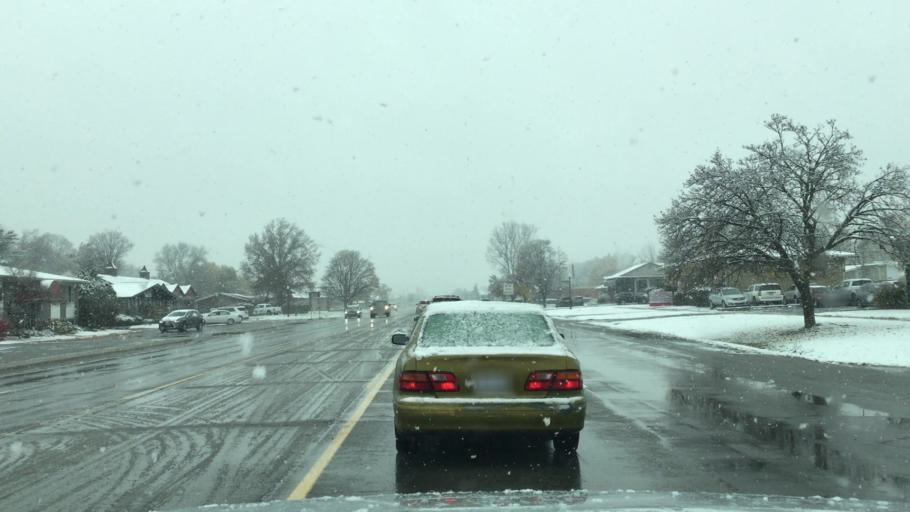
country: US
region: Michigan
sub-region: Oakland County
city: Lathrup Village
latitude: 42.4962
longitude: -83.2222
